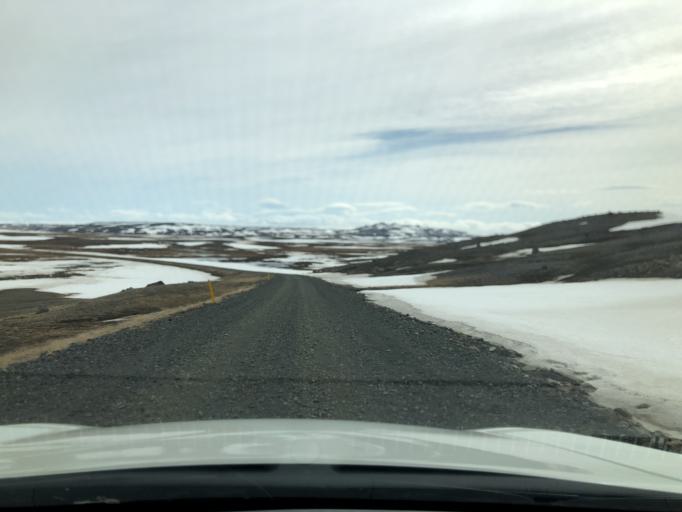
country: IS
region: East
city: Egilsstadir
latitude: 65.3071
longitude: -15.3561
